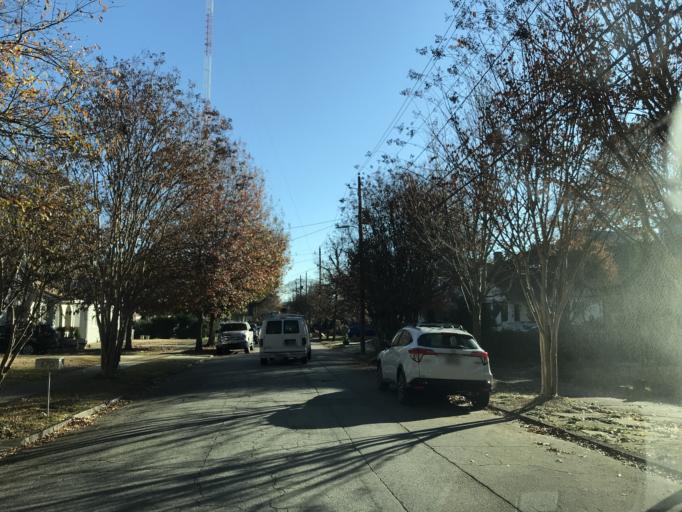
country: US
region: Georgia
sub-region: Fulton County
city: Atlanta
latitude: 33.7639
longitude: -84.3655
